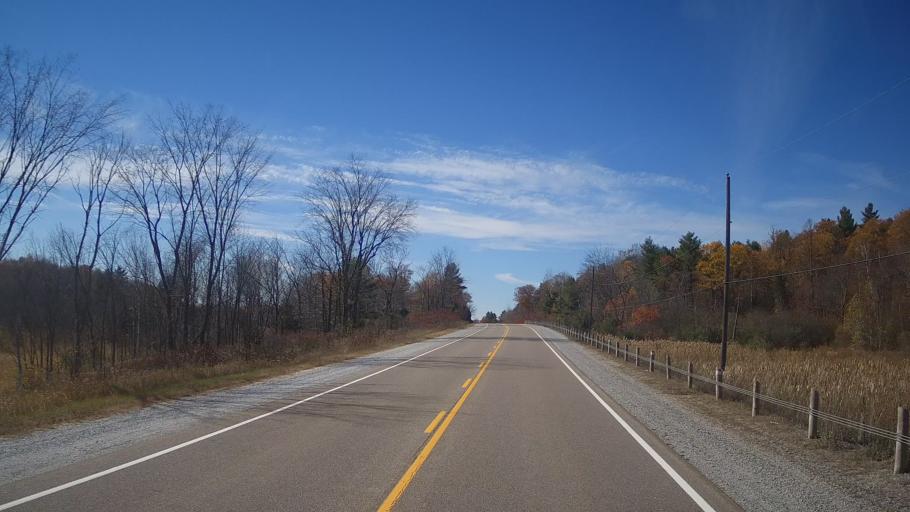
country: CA
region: Ontario
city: Perth
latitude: 44.8398
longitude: -76.5085
